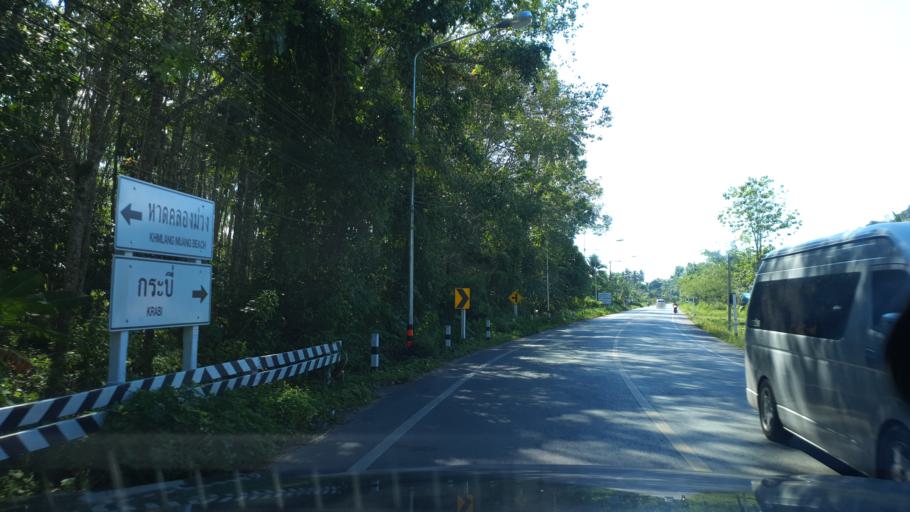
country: TH
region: Phangnga
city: Ban Ao Nang
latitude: 8.0697
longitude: 98.8089
